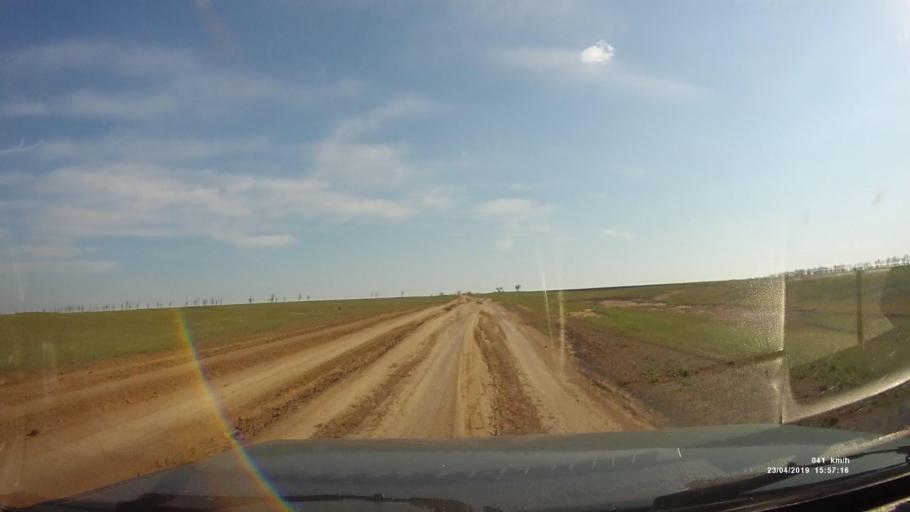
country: RU
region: Rostov
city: Remontnoye
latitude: 46.5328
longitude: 43.1102
